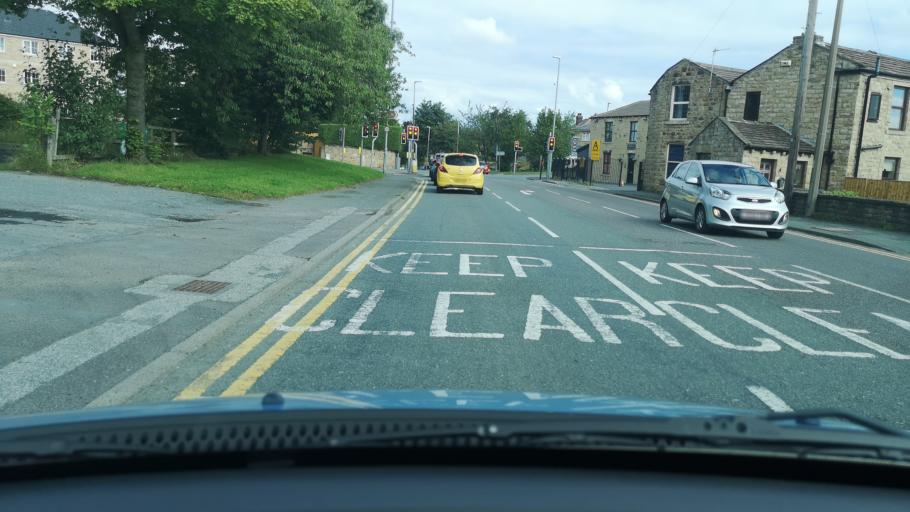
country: GB
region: England
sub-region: Kirklees
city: Liversedge
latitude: 53.6997
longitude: -1.6961
